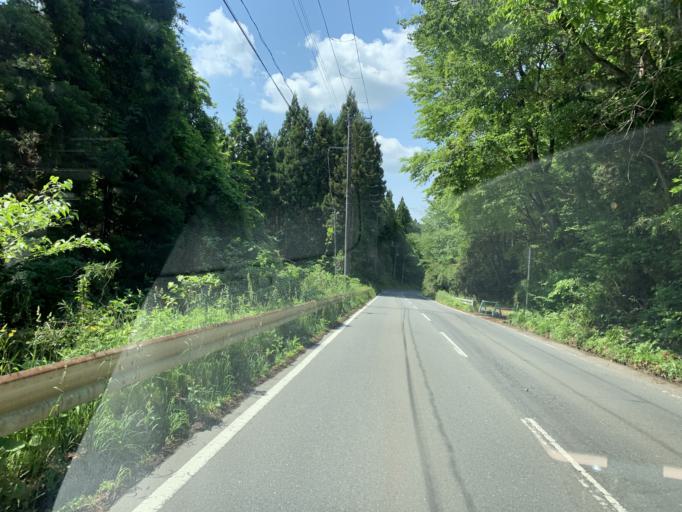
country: JP
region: Miyagi
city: Furukawa
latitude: 38.7119
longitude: 140.9420
